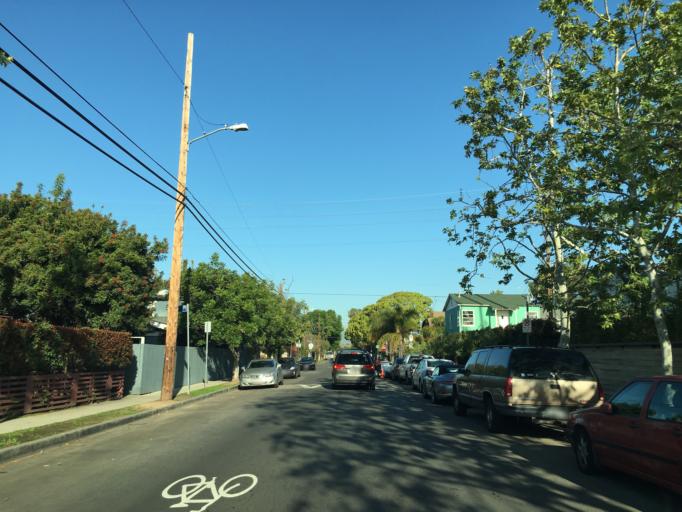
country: US
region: California
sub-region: Los Angeles County
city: Marina del Rey
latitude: 33.9927
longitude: -118.4590
